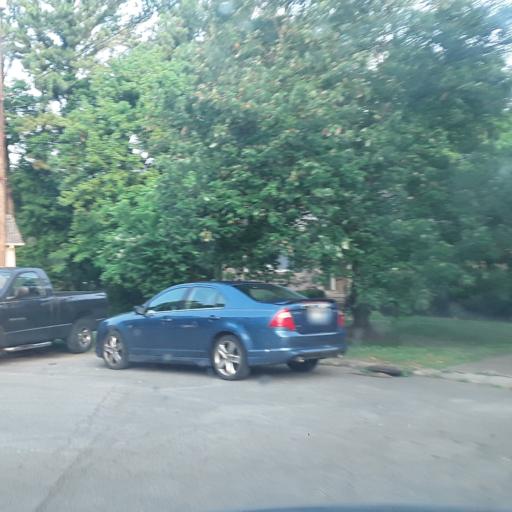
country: US
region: Tennessee
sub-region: Williamson County
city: Brentwood
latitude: 36.0523
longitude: -86.7356
